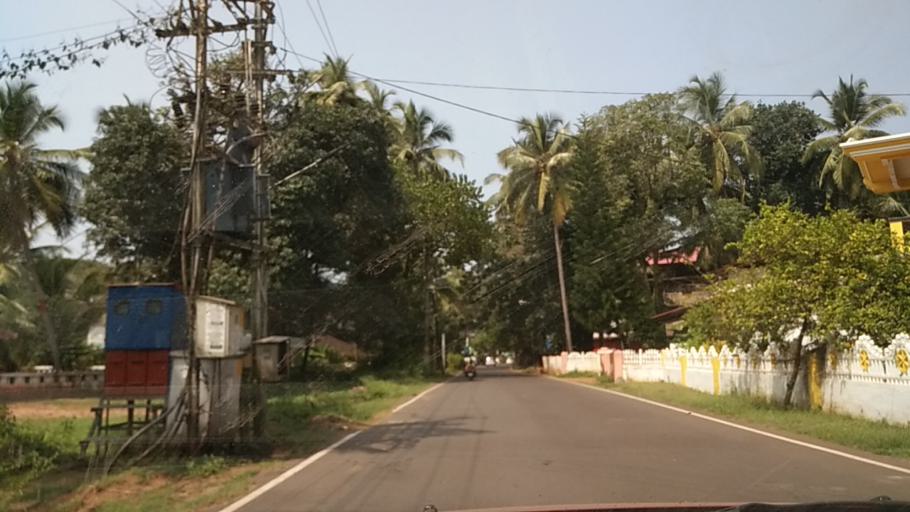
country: IN
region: Goa
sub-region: South Goa
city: Colva
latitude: 15.3263
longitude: 73.9040
